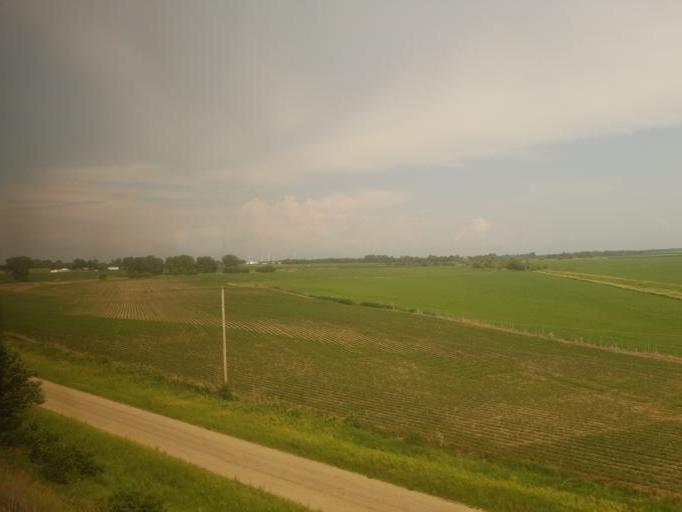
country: US
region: Illinois
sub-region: Henry County
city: Kewanee
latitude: 41.3151
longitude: -89.6980
